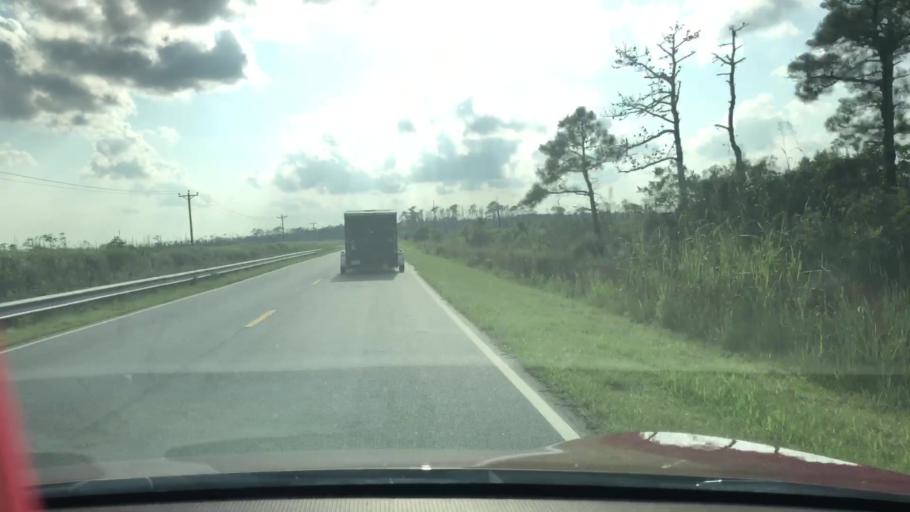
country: US
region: North Carolina
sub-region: Dare County
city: Wanchese
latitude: 35.6080
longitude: -75.8086
